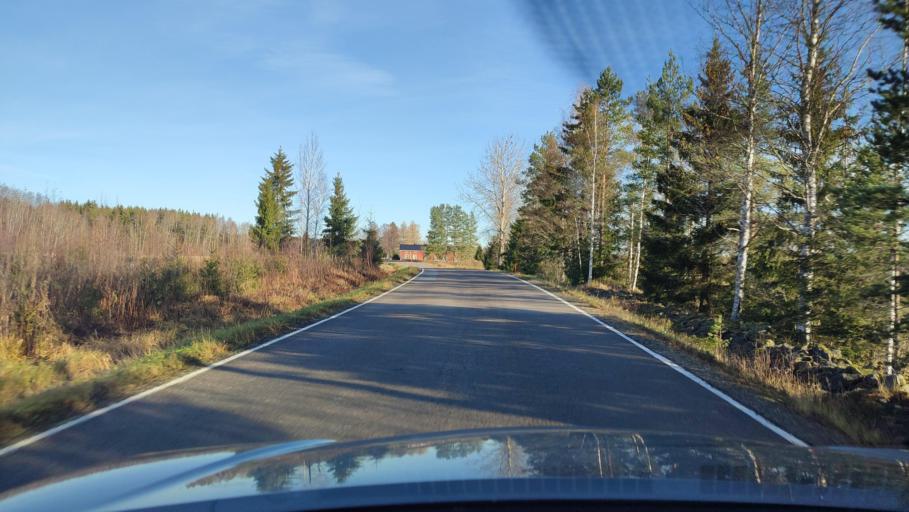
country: FI
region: Southern Ostrobothnia
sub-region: Suupohja
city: Karijoki
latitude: 62.3613
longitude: 21.6995
